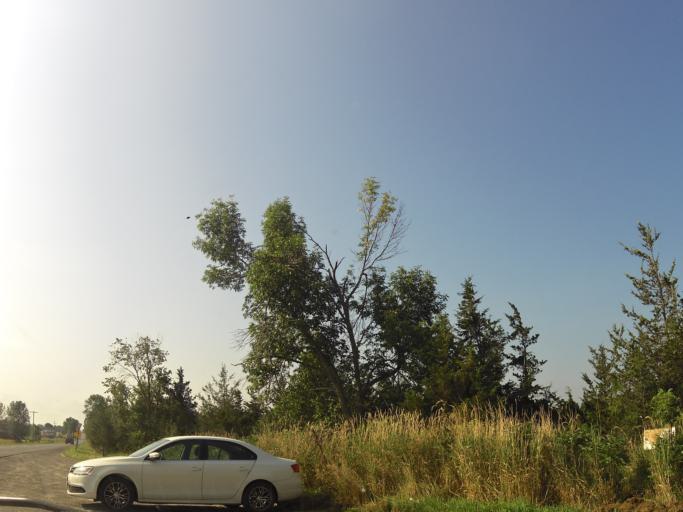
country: CA
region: Ontario
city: Deseronto
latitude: 44.2417
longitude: -77.0623
